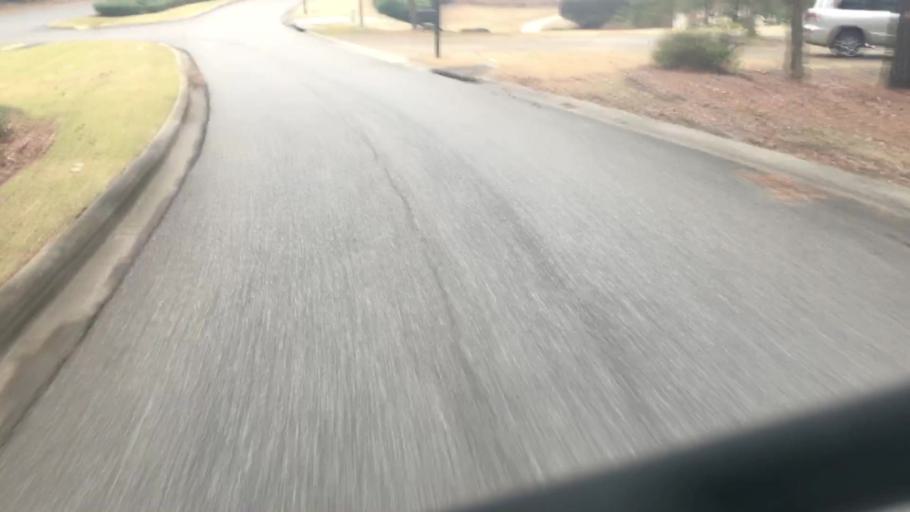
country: US
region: Alabama
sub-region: Shelby County
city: Indian Springs Village
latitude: 33.3543
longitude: -86.8049
